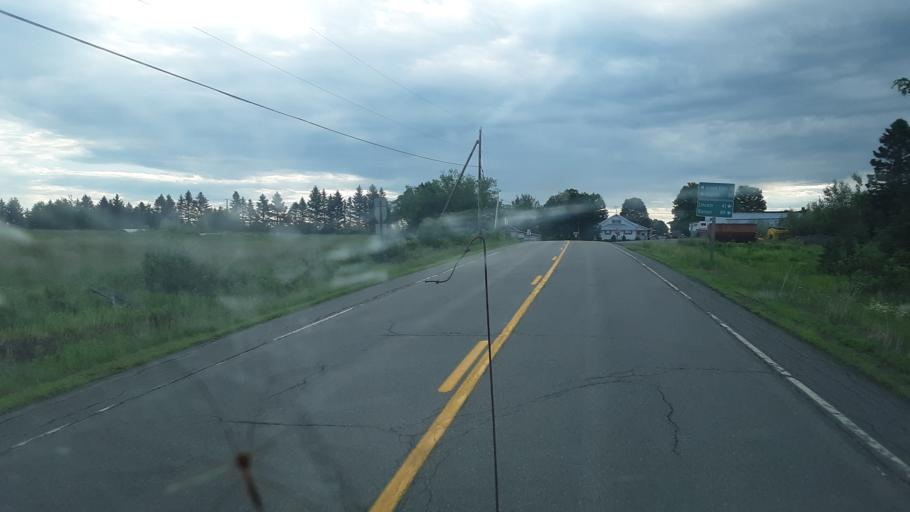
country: US
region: Maine
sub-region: Penobscot County
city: Patten
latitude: 45.8706
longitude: -68.3321
